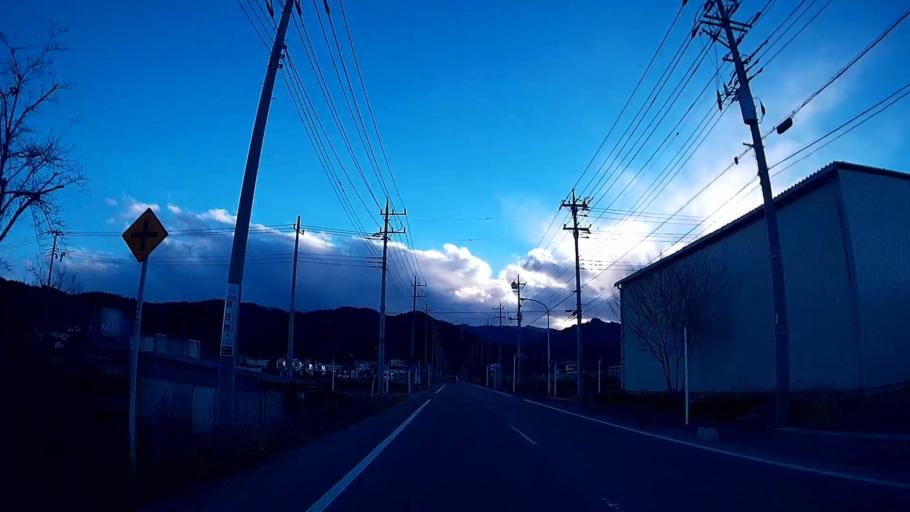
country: JP
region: Saitama
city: Chichibu
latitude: 36.0263
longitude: 138.9865
